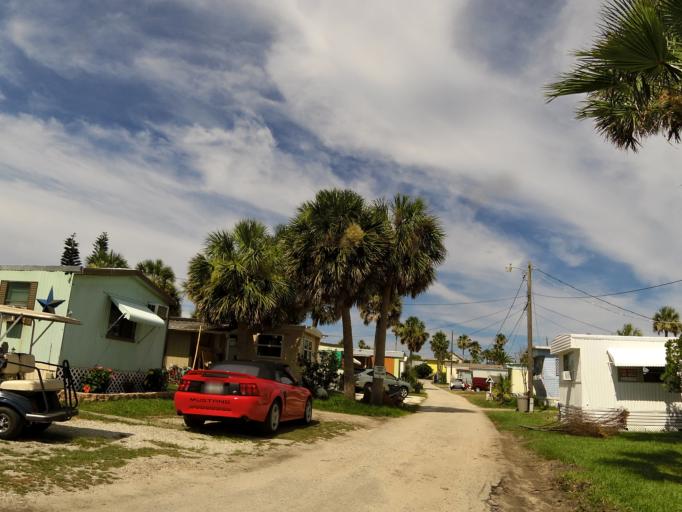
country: US
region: Florida
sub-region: Flagler County
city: Flagler Beach
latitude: 29.4770
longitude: -81.1290
